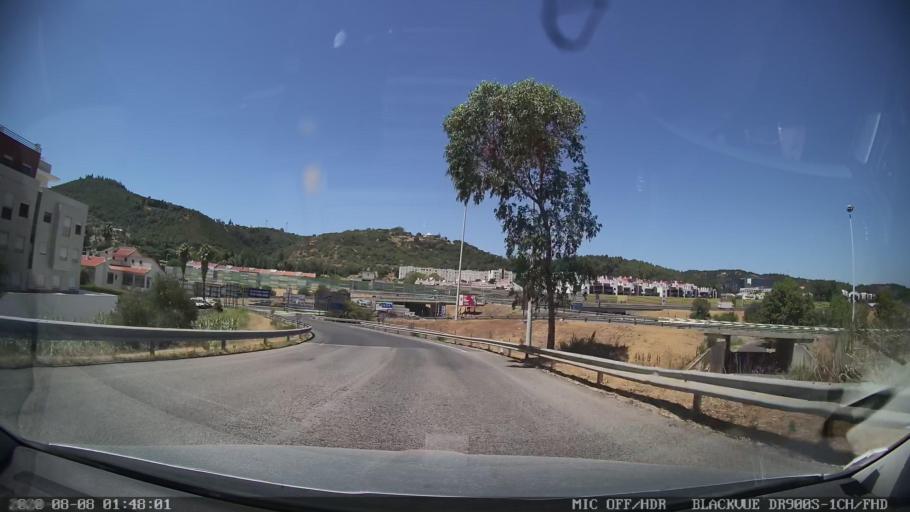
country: PT
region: Lisbon
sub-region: Vila Franca de Xira
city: Vila Franca de Xira
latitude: 38.9684
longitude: -8.9809
